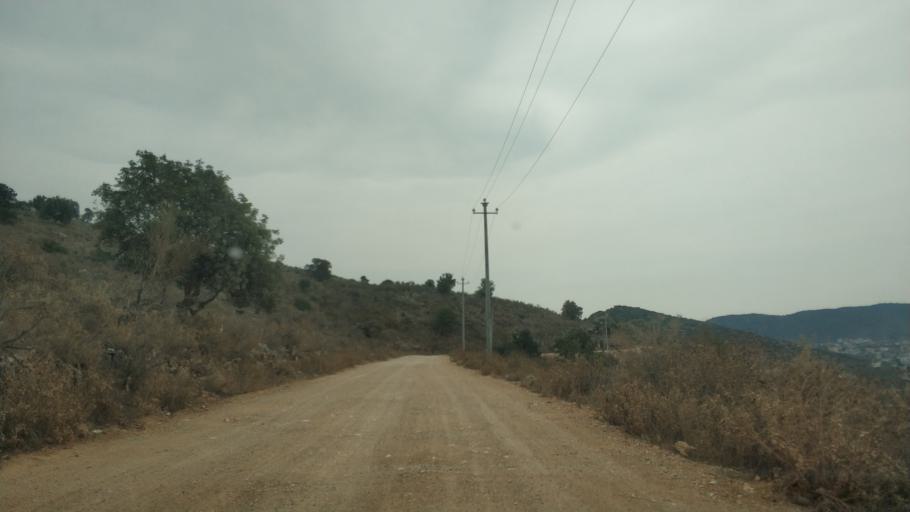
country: AL
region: Vlore
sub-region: Rrethi i Sarandes
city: Sarande
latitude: 39.7943
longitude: 20.0039
